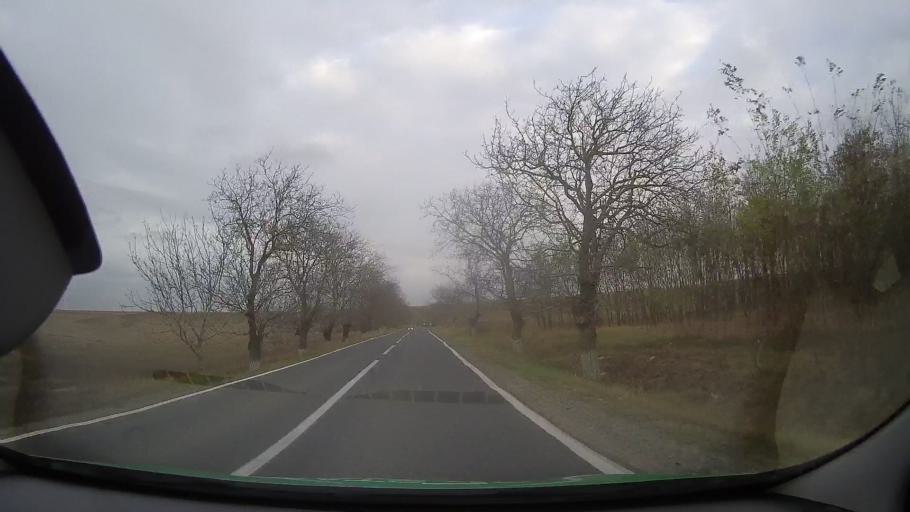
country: RO
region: Constanta
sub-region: Comuna Adamclisi
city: Adamclisi
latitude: 44.0879
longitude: 27.9737
